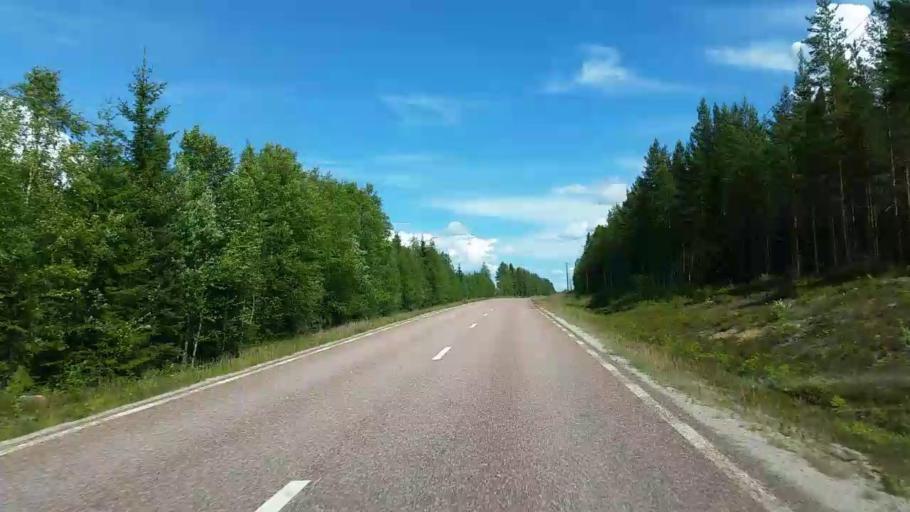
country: SE
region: Dalarna
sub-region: Rattviks Kommun
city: Raettvik
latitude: 61.1892
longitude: 15.3131
